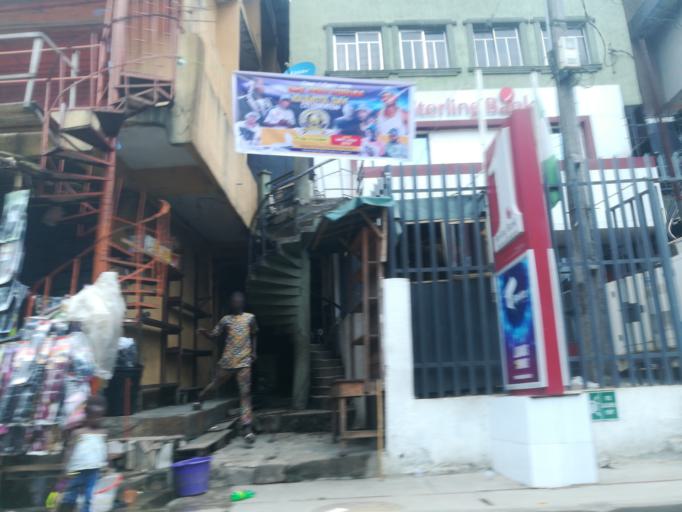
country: NG
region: Lagos
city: Lagos
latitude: 6.4594
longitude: 3.3876
